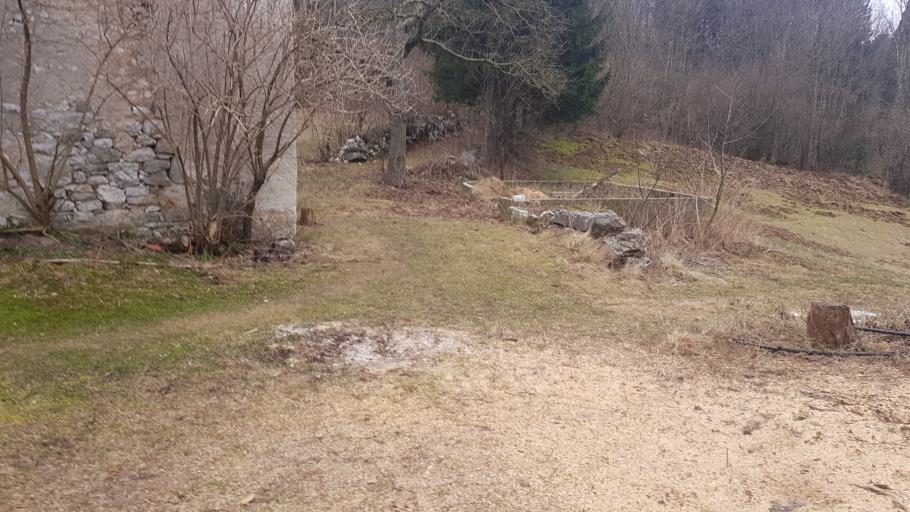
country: SI
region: Nova Gorica
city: Kromberk
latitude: 46.0223
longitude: 13.7015
